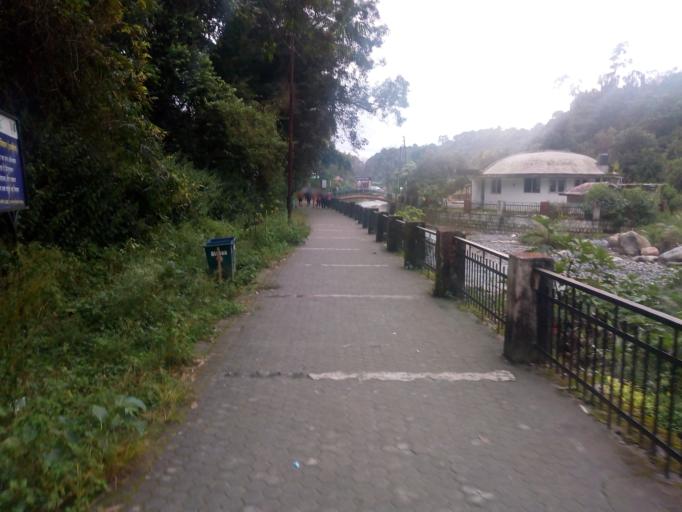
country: IN
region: Uttarakhand
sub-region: Dehradun
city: Dehradun
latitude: 30.3764
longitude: 78.0606
